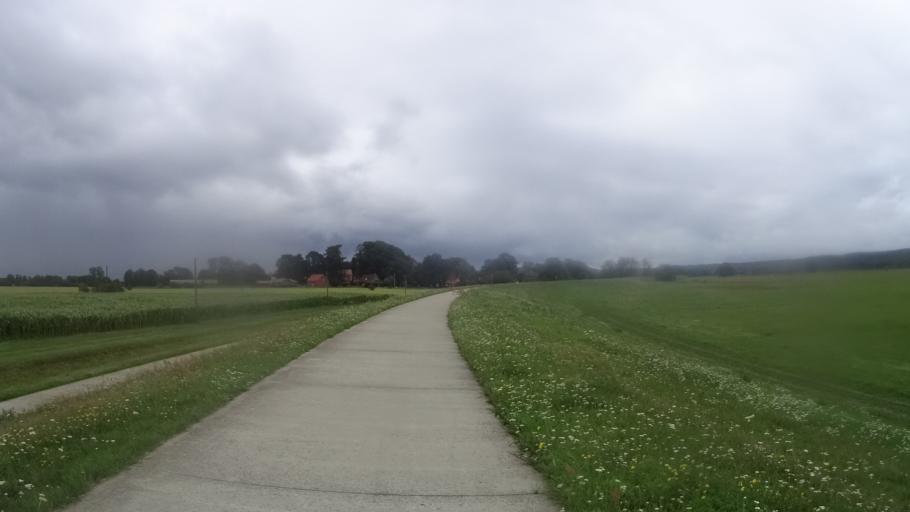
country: DE
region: Lower Saxony
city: Tosterglope
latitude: 53.2764
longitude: 10.8255
